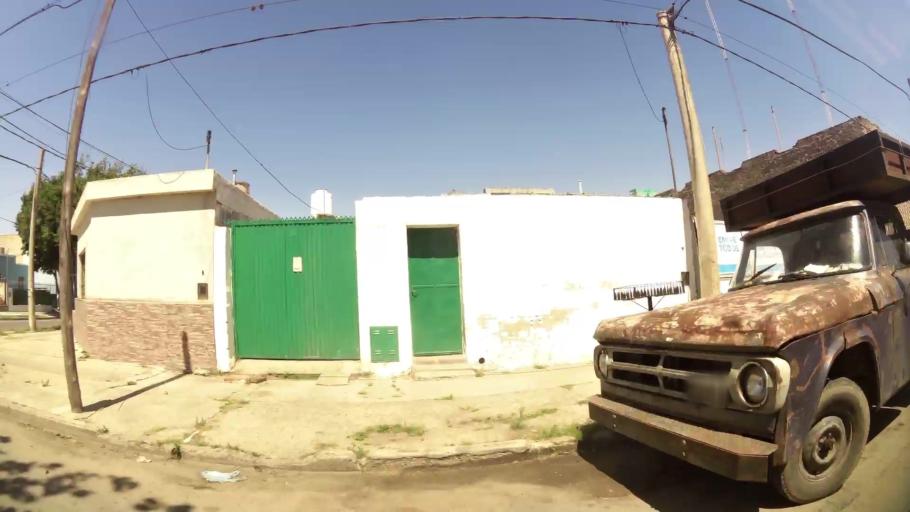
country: AR
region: Cordoba
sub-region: Departamento de Capital
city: Cordoba
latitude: -31.3791
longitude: -64.1546
